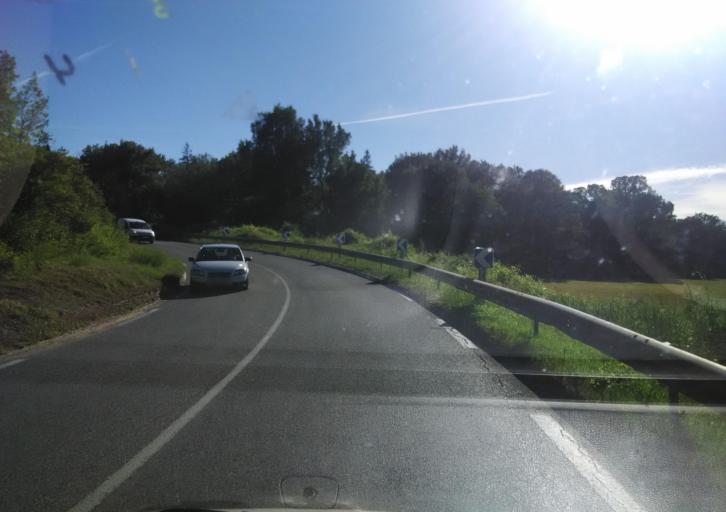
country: FR
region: Provence-Alpes-Cote d'Azur
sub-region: Departement du Var
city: Vinon-sur-Verdon
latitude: 43.7169
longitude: 5.7884
